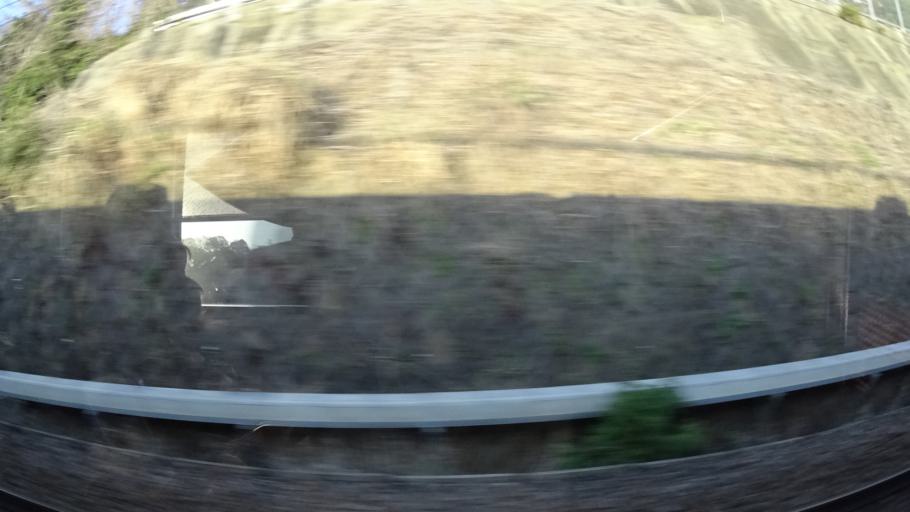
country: JP
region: Kanagawa
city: Yokohama
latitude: 35.3776
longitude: 139.6191
